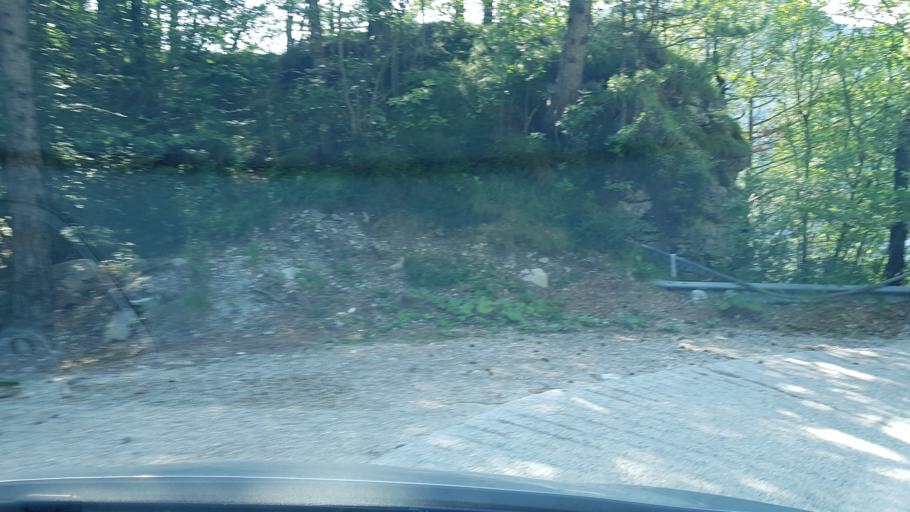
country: IT
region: Friuli Venezia Giulia
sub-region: Provincia di Udine
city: Moggio Udinese
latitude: 46.4337
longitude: 13.2109
